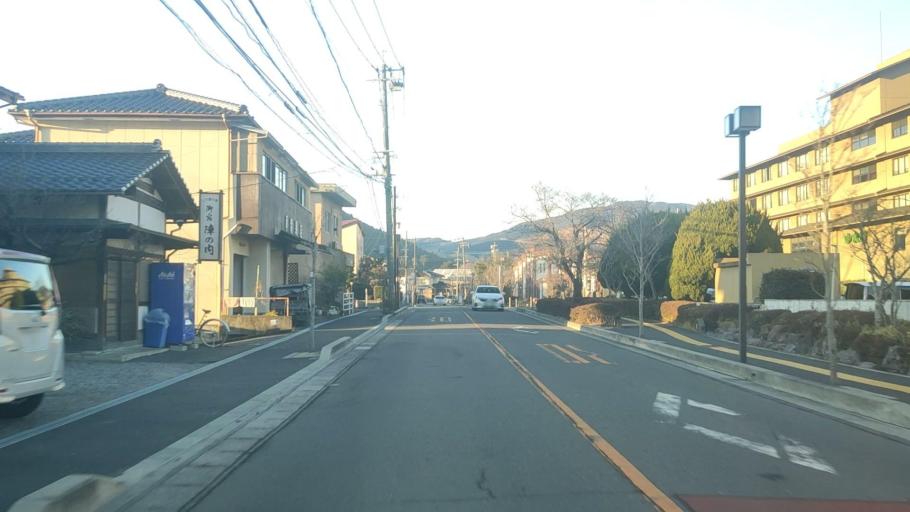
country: JP
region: Oita
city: Beppu
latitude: 33.2586
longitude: 131.3567
